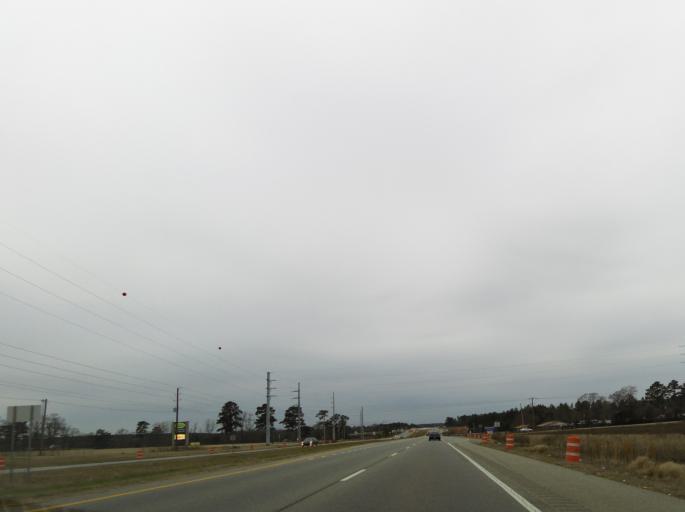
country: US
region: Georgia
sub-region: Houston County
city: Perry
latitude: 32.5465
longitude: -83.7368
